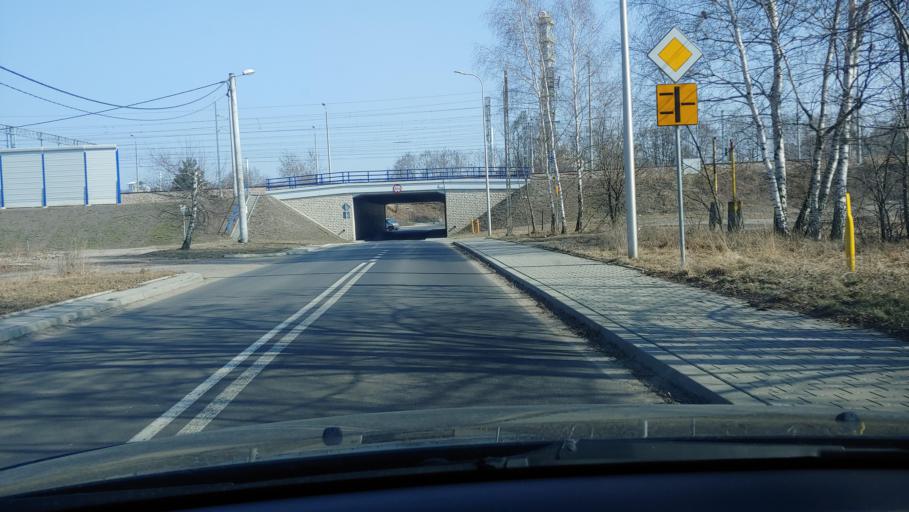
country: PL
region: Lesser Poland Voivodeship
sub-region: Powiat chrzanowski
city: Trzebinia
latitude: 50.1549
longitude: 19.4477
